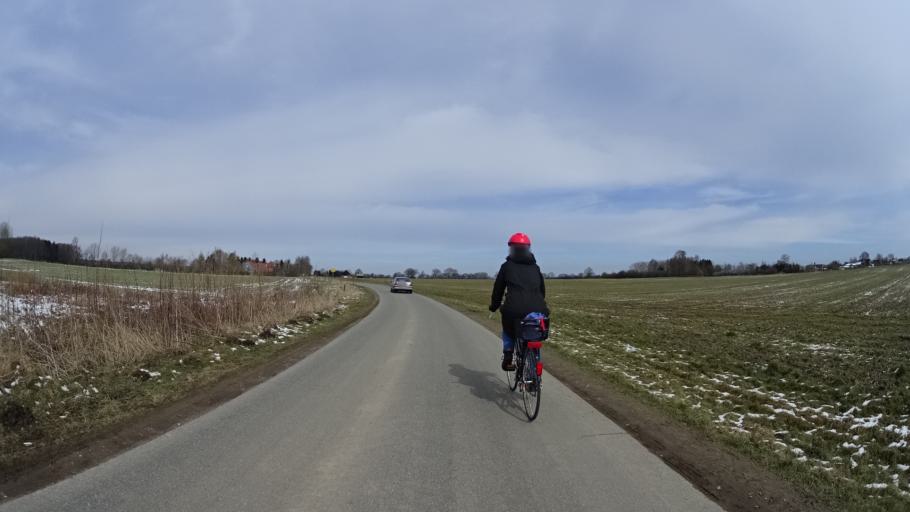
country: DE
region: Schleswig-Holstein
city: Rendswuhren
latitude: 54.0863
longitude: 10.1999
